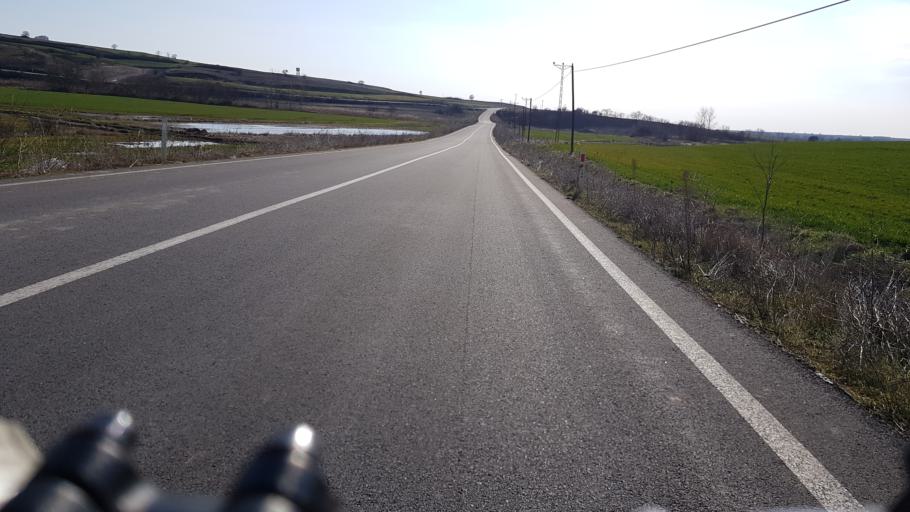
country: TR
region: Tekirdag
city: Velimese
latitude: 41.3596
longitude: 27.8532
